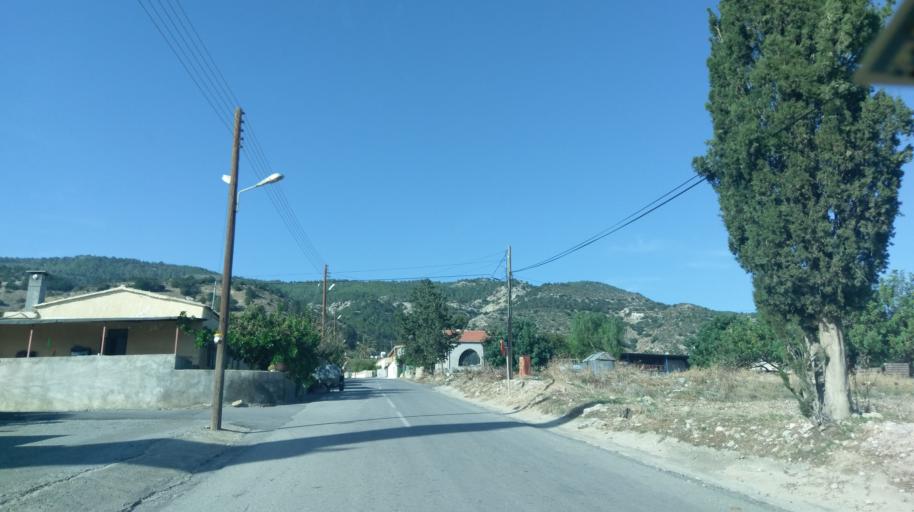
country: CY
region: Ammochostos
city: Trikomo
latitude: 35.3454
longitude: 33.8001
